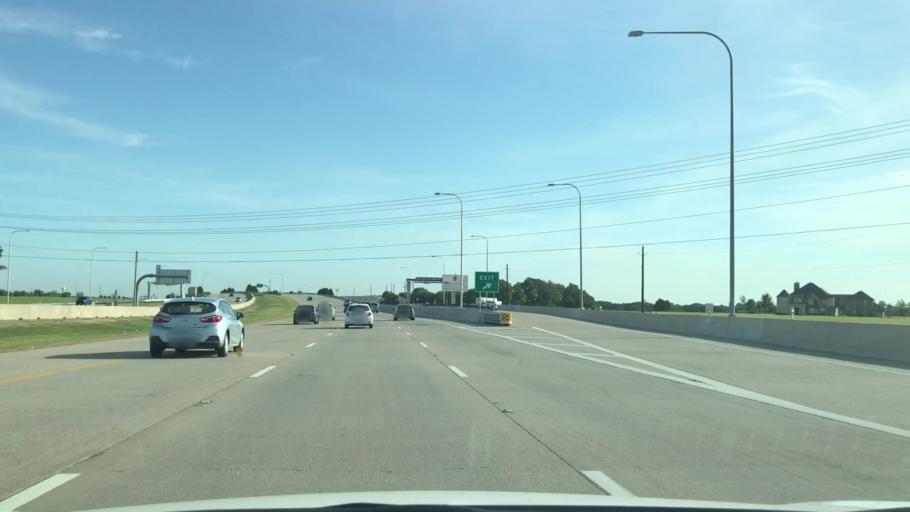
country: US
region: Texas
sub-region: Dallas County
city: Rowlett
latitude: 32.9266
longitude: -96.5525
